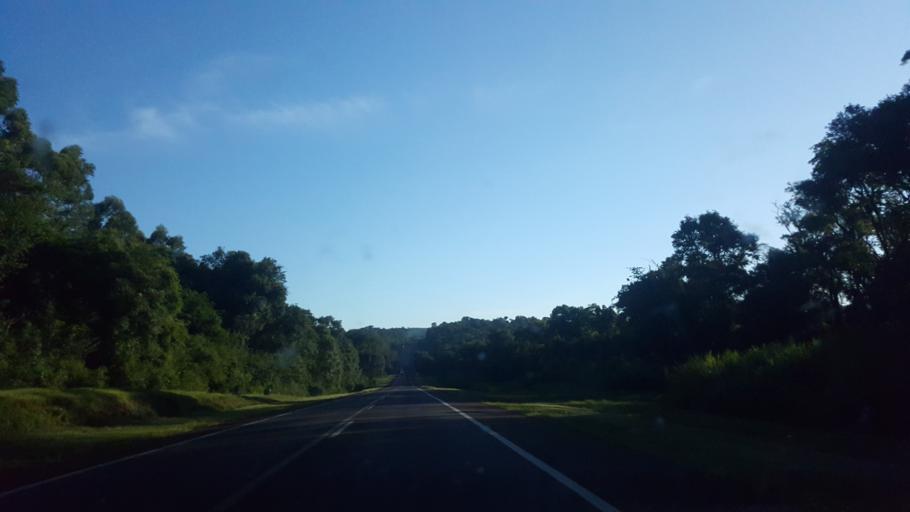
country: AR
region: Misiones
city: El Alcazar
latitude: -26.7044
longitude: -54.8419
